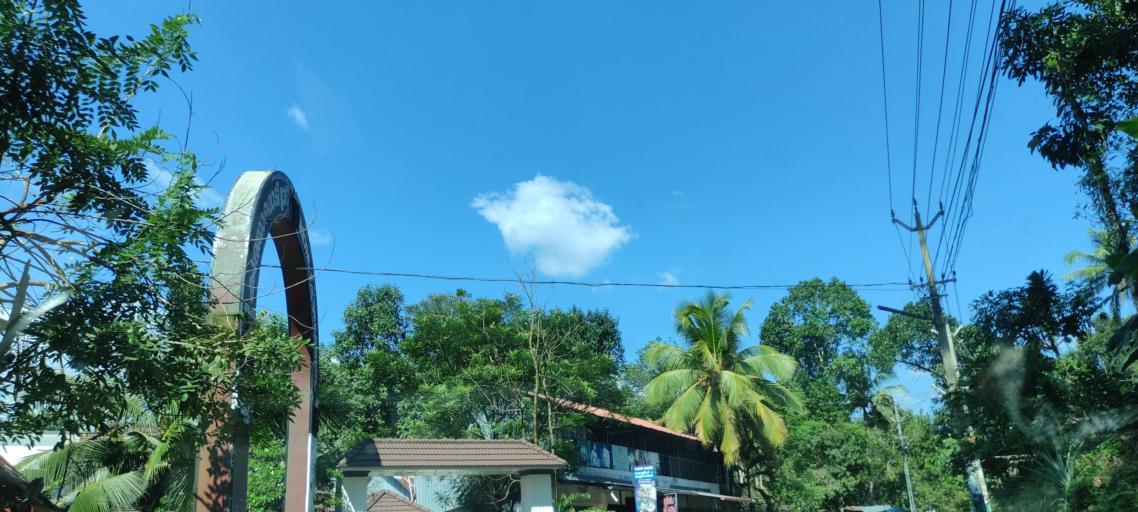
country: IN
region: Kerala
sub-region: Pattanamtitta
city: Adur
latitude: 9.1131
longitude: 76.7297
